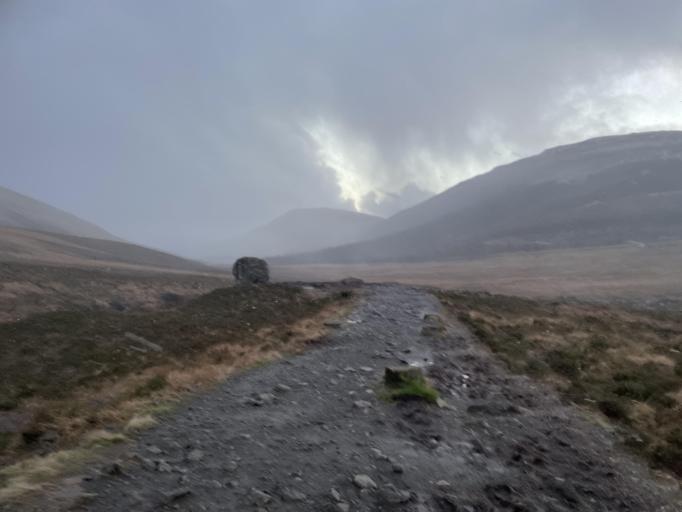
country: GB
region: Scotland
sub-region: Highland
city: Isle of Skye
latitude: 57.2499
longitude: -6.2653
